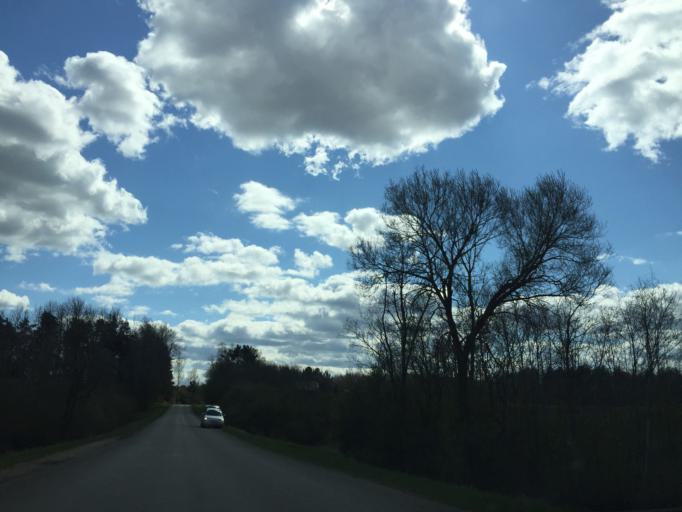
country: LV
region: Rezekne
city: Rezekne
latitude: 56.5485
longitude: 27.1503
